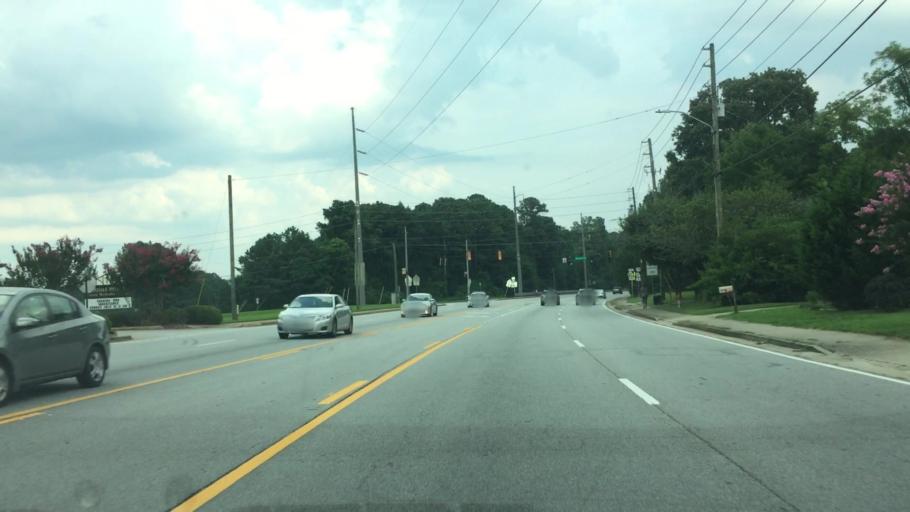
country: US
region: Georgia
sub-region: DeKalb County
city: Avondale Estates
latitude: 33.7736
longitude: -84.2578
